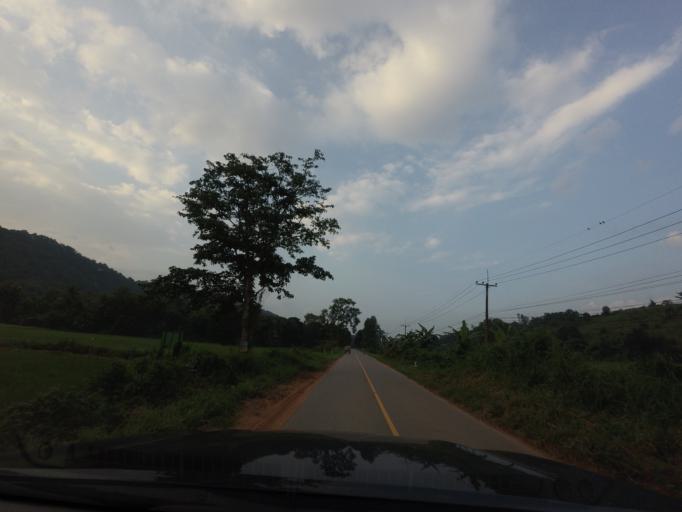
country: TH
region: Loei
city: Na Haeo
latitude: 17.3903
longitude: 101.0458
